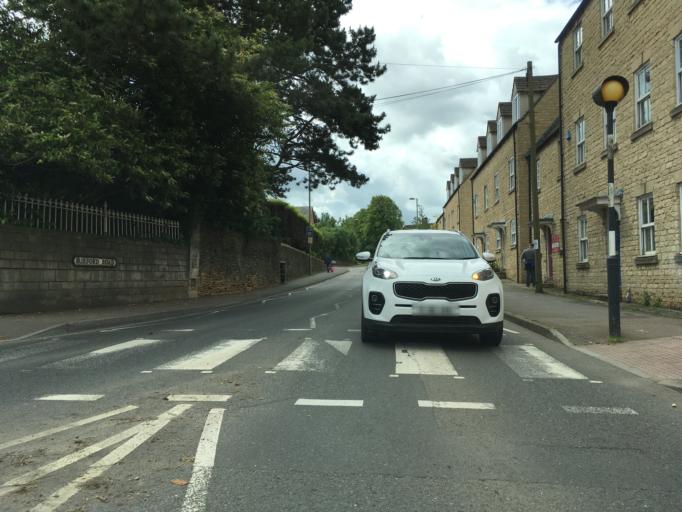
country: GB
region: England
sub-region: Oxfordshire
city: Chipping Norton
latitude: 51.9395
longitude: -1.5455
